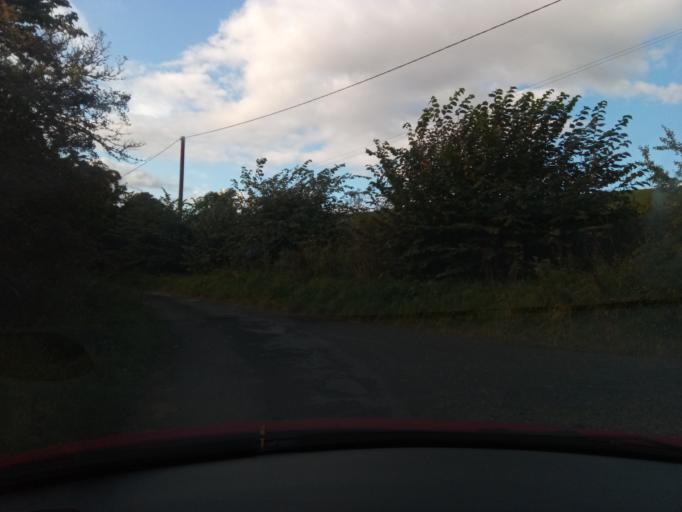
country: GB
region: Scotland
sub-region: The Scottish Borders
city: Kelso
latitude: 55.5267
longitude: -2.3481
